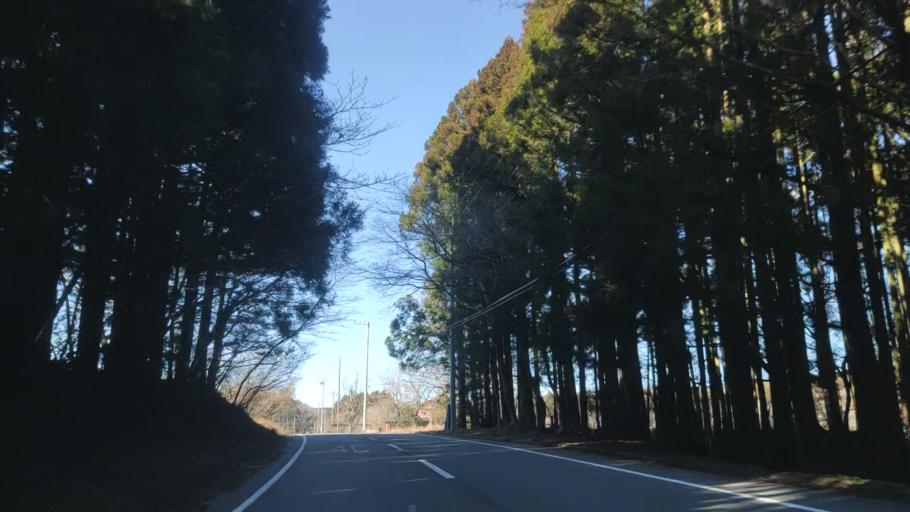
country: JP
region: Shizuoka
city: Fujinomiya
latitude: 35.3613
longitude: 138.6057
